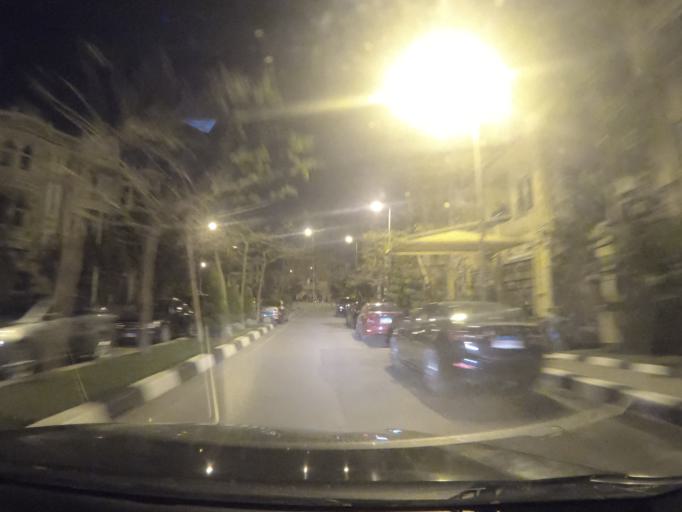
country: EG
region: Muhafazat al Qahirah
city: Cairo
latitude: 30.0146
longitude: 31.4262
